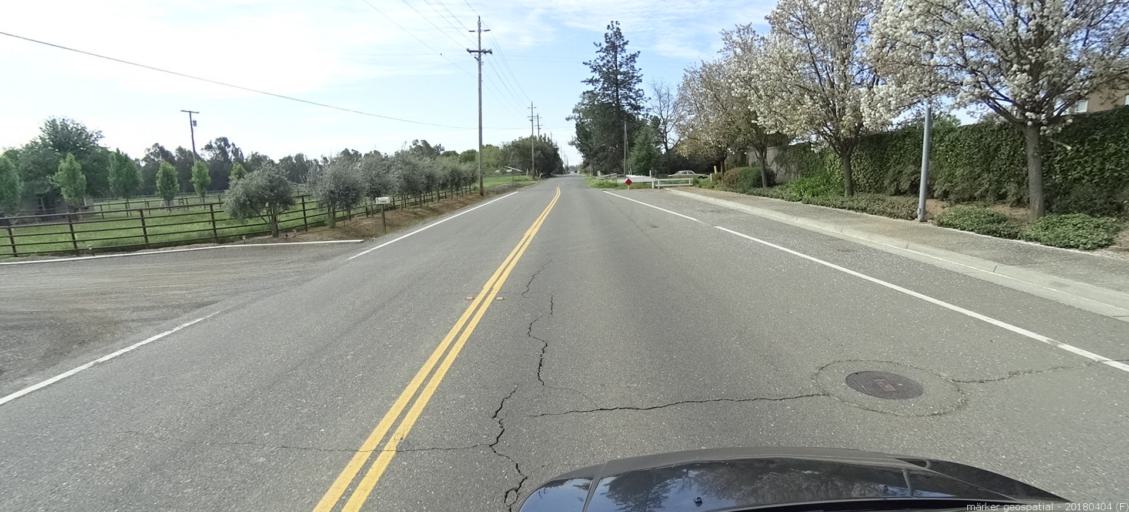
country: US
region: California
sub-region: Sacramento County
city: Galt
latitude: 38.2673
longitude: -121.2827
